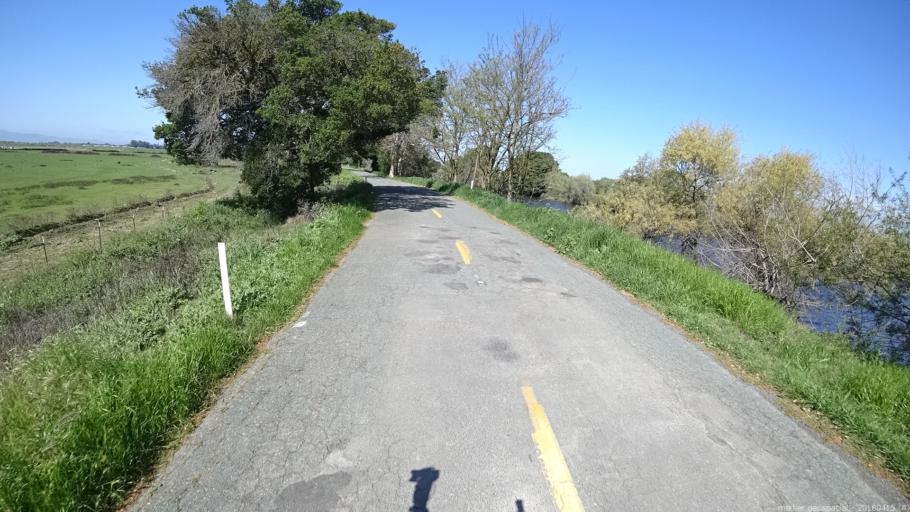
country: US
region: California
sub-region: Solano County
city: Rio Vista
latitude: 38.1235
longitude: -121.6660
